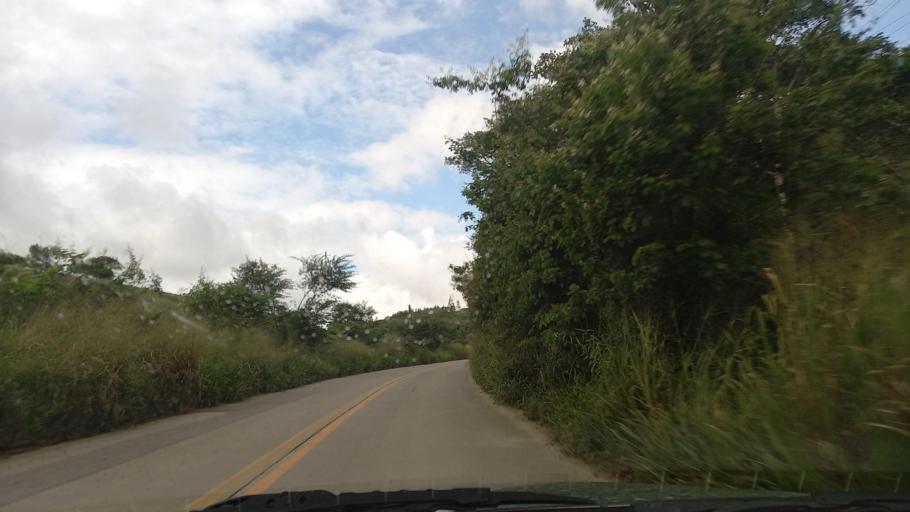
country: BR
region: Pernambuco
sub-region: Quipapa
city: Quipapa
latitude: -8.7874
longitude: -35.9753
